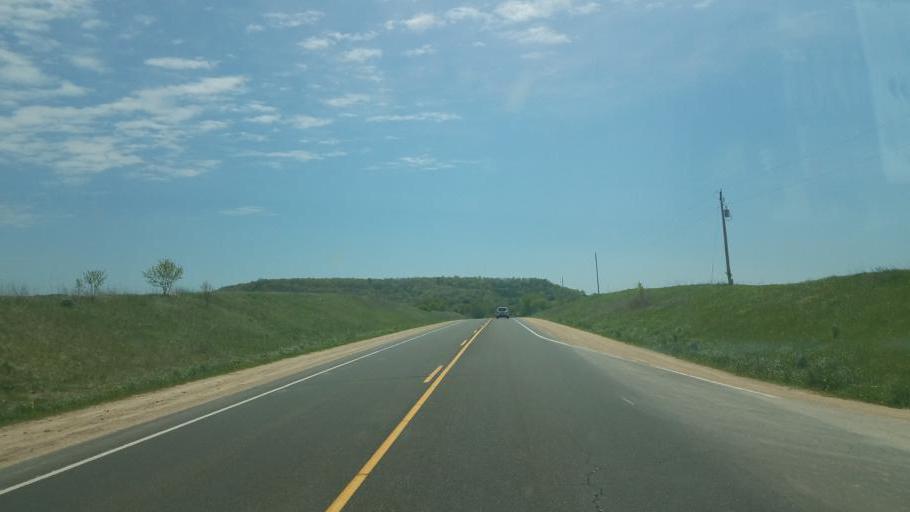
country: US
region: Wisconsin
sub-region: Monroe County
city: Tomah
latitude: 43.8385
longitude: -90.4740
